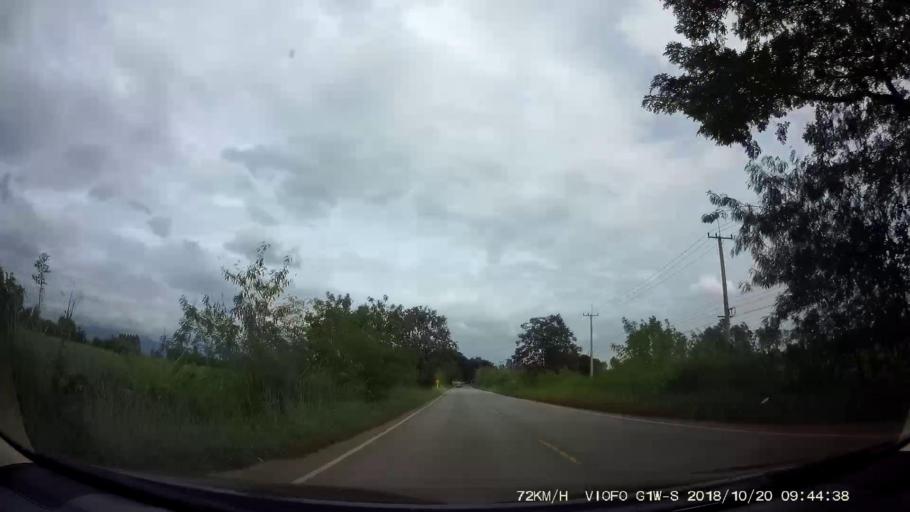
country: TH
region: Chaiyaphum
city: Khon San
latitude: 16.4852
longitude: 101.9429
